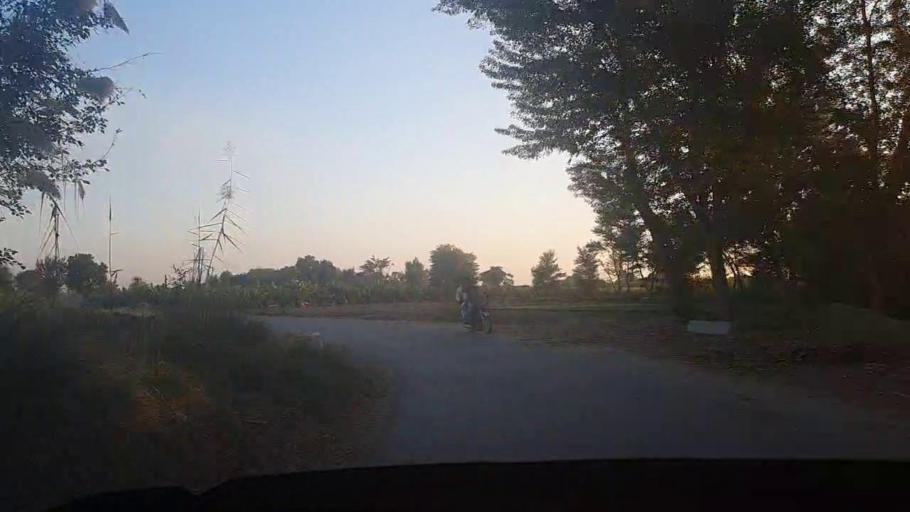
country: PK
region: Sindh
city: Sobhadero
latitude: 27.3481
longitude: 68.3754
